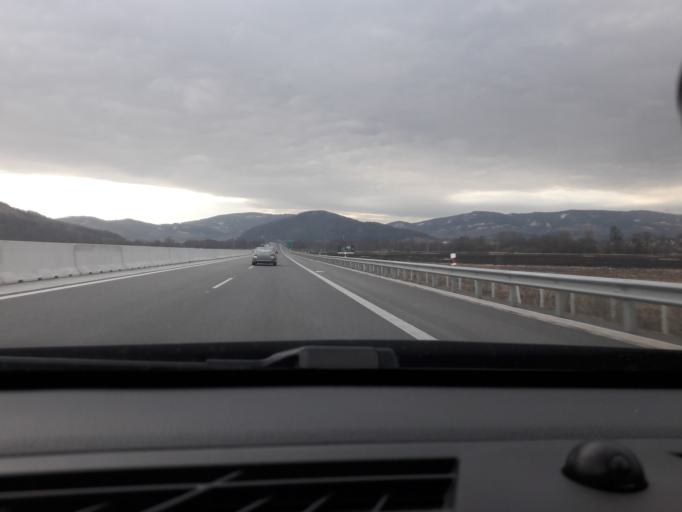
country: SK
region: Banskobystricky
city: Hrochot,Slovakia
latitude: 48.5605
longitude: 19.3152
